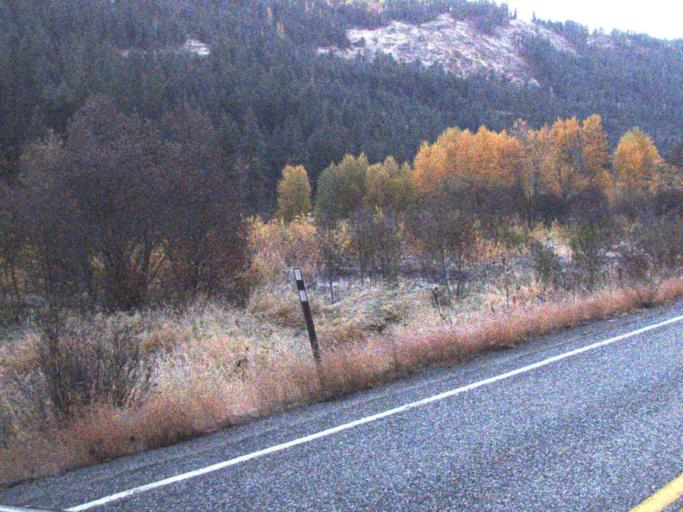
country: US
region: Washington
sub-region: Ferry County
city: Republic
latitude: 48.3852
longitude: -118.7484
